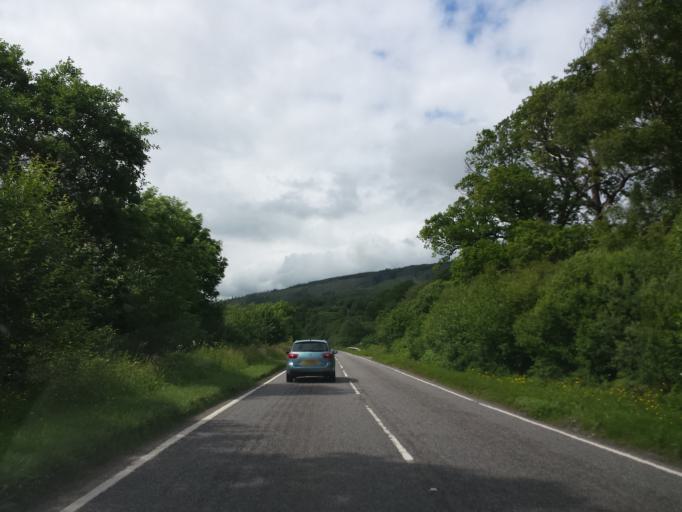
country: GB
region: Scotland
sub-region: Highland
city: Fort William
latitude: 56.8515
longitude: -5.1715
